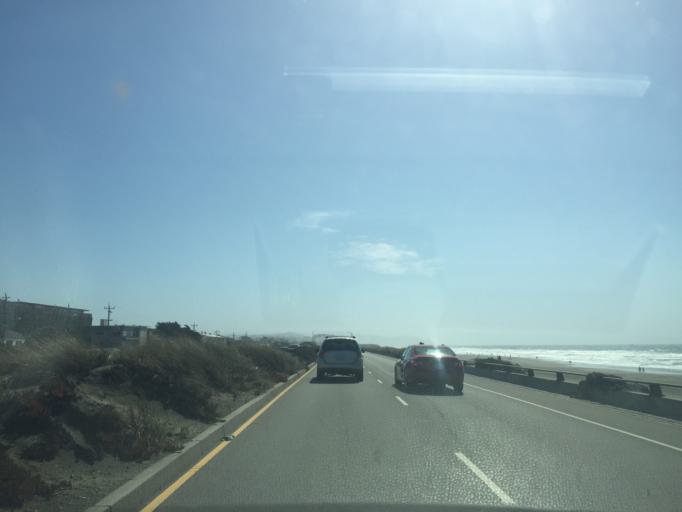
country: US
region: California
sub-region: San Mateo County
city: Daly City
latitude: 37.7486
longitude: -122.5084
